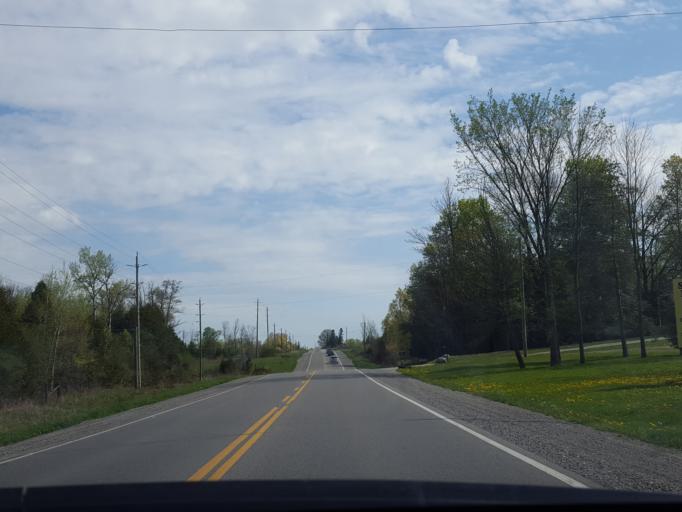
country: CA
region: Ontario
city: Uxbridge
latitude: 44.1476
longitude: -78.9052
